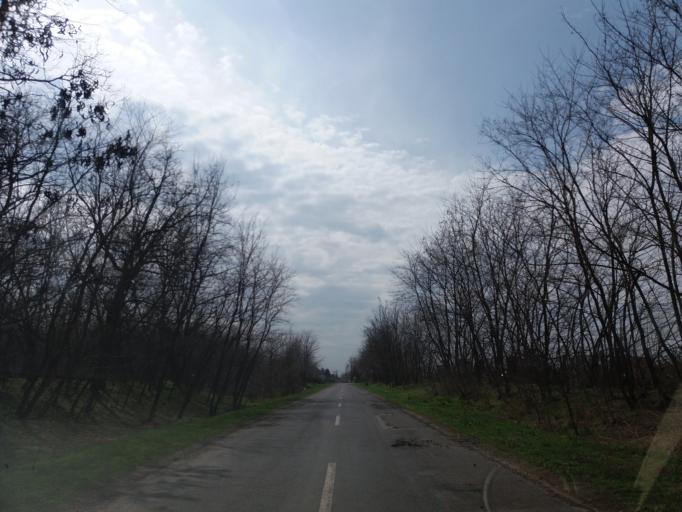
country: HU
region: Szabolcs-Szatmar-Bereg
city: Petnehaza
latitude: 48.0532
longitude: 22.0463
